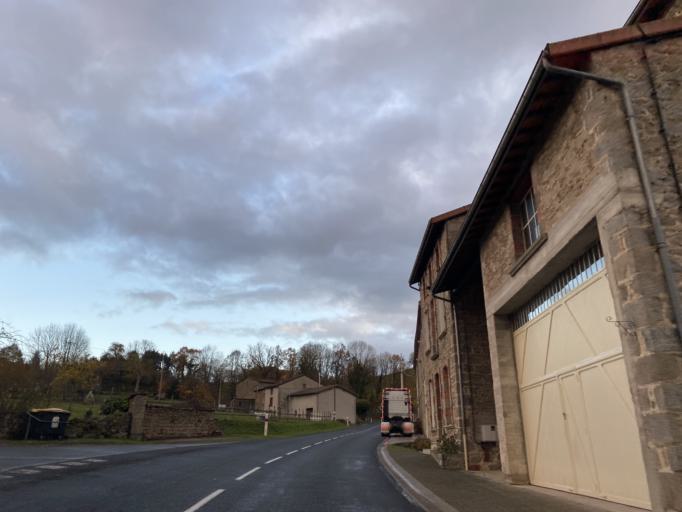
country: FR
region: Auvergne
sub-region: Departement du Puy-de-Dome
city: Cunlhat
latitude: 45.6927
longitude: 3.5779
